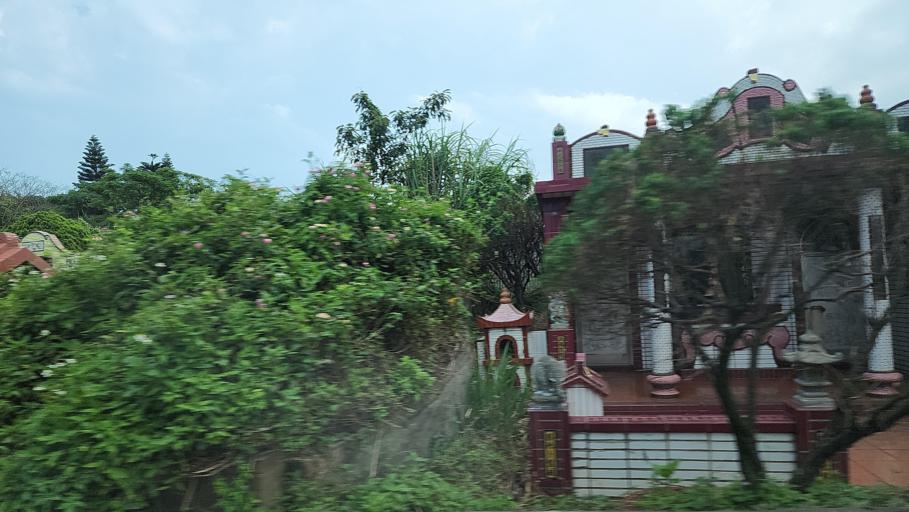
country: TW
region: Taiwan
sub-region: Keelung
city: Keelung
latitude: 25.2266
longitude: 121.6389
